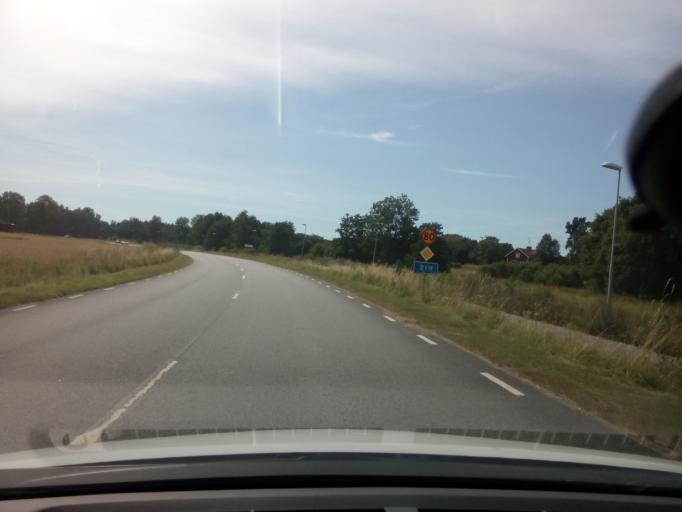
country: SE
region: Soedermanland
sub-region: Nykopings Kommun
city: Nykoping
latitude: 58.7760
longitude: 17.0750
